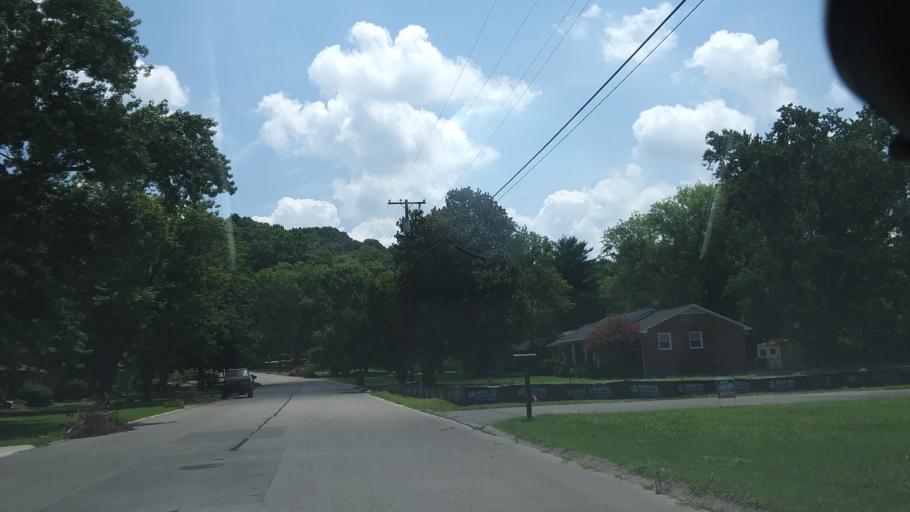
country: US
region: Tennessee
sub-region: Davidson County
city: Belle Meade
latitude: 36.0840
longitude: -86.9410
